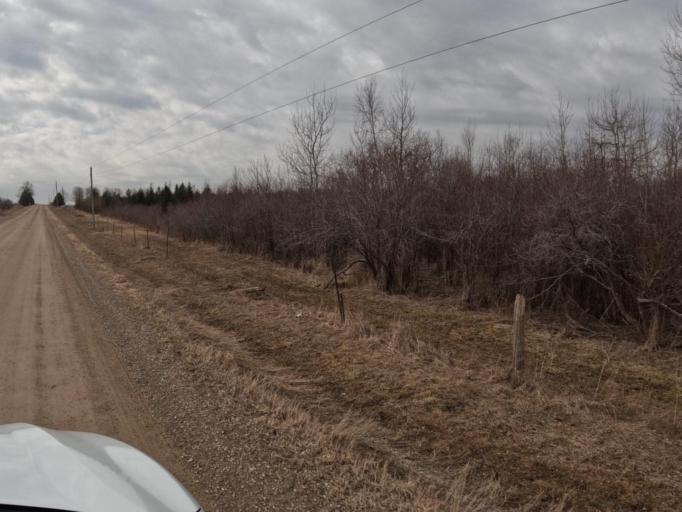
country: CA
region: Ontario
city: Orangeville
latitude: 43.9340
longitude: -80.1887
